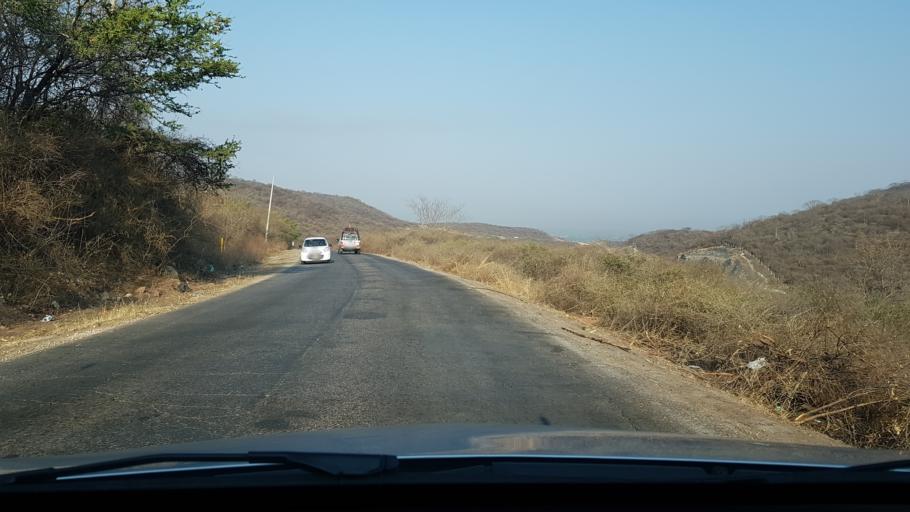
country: MX
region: Morelos
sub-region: Tlaltizapan de Zapata
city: Colonia Palo Prieto (Chipitongo)
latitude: 18.6755
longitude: -99.0647
